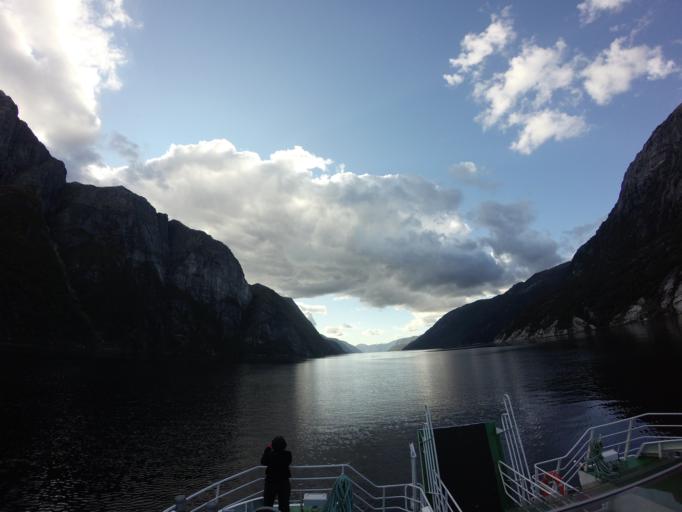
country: NO
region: Vest-Agder
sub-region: Sirdal
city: Tonstad
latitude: 59.0369
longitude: 6.5448
